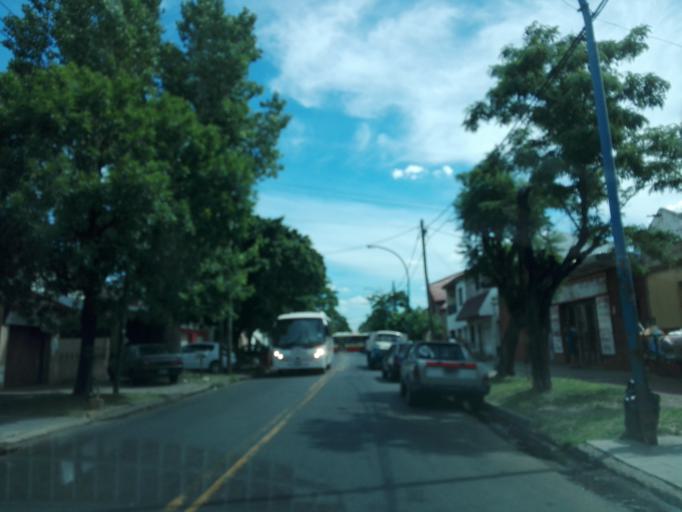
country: AR
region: Buenos Aires
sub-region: Partido de Lanus
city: Lanus
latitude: -34.7083
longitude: -58.3735
